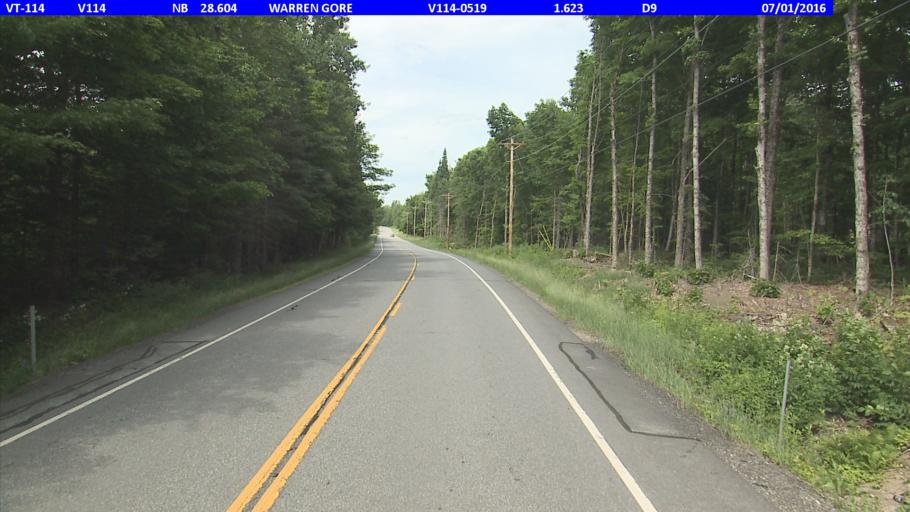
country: CA
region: Quebec
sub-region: Estrie
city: Coaticook
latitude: 44.9073
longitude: -71.8769
